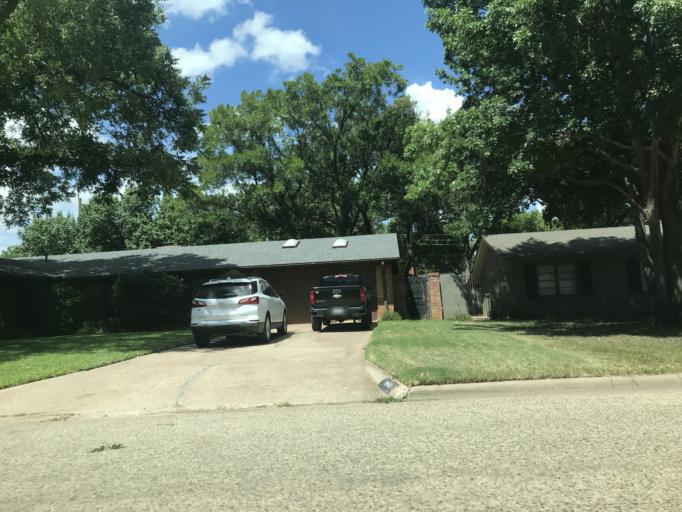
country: US
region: Texas
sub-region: Taylor County
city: Abilene
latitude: 32.4234
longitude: -99.7682
